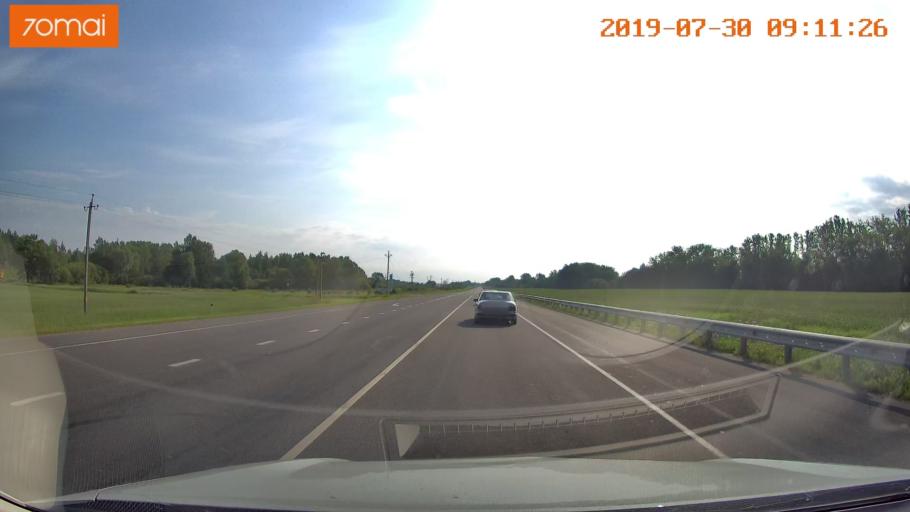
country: RU
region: Kaliningrad
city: Nesterov
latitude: 54.6128
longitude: 22.4497
